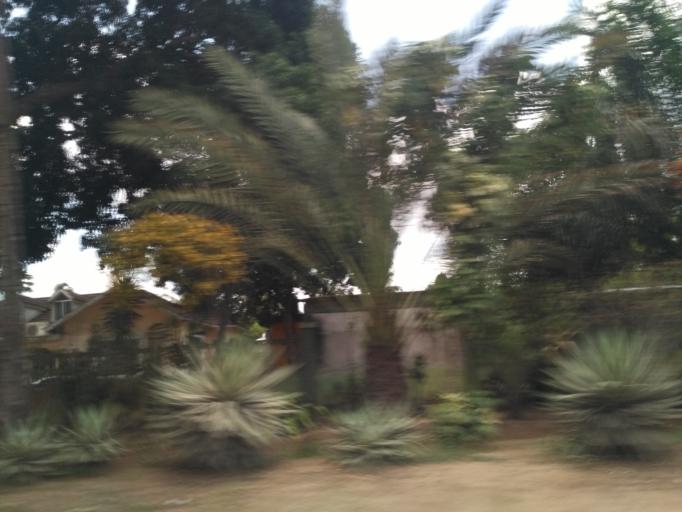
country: TZ
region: Dar es Salaam
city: Dar es Salaam
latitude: -6.8564
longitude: 39.3547
